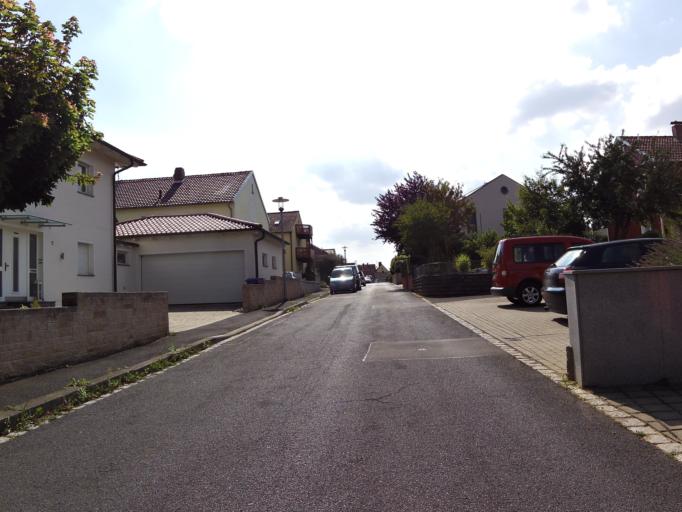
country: DE
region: Bavaria
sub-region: Regierungsbezirk Unterfranken
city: Estenfeld
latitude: 49.8290
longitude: 10.0018
